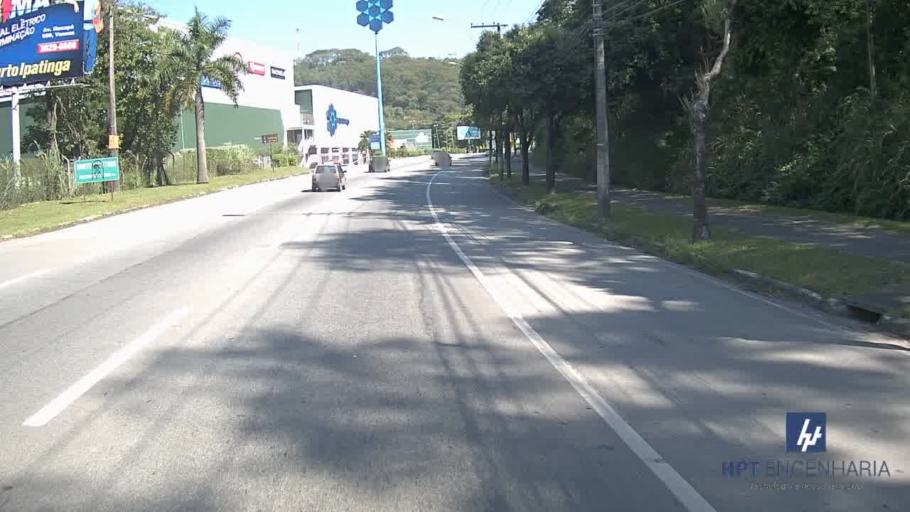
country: BR
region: Minas Gerais
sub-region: Ipatinga
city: Ipatinga
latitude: -19.4940
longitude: -42.5651
